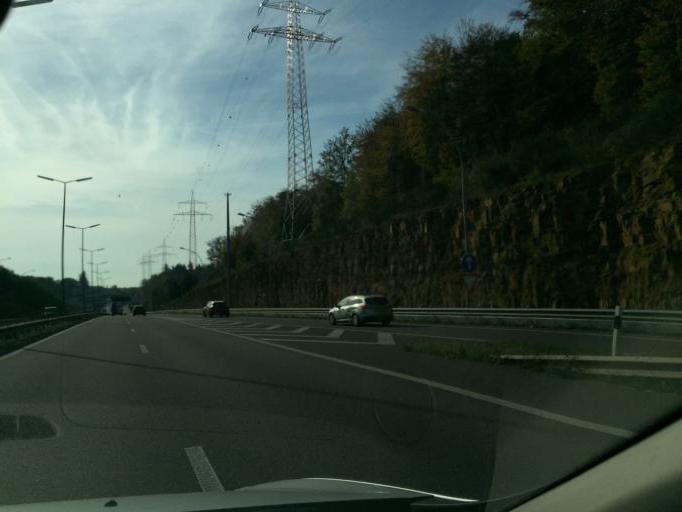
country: LU
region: Luxembourg
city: Helmsange
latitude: 49.6504
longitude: 6.1859
